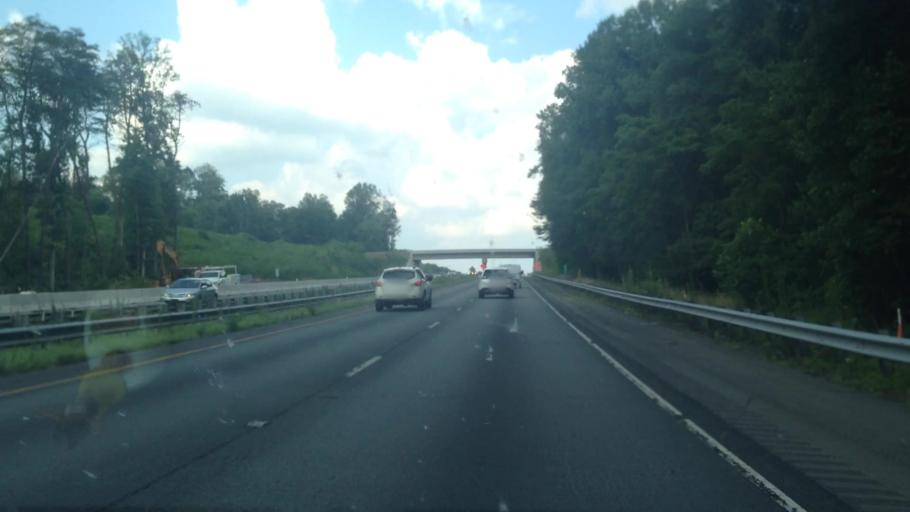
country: US
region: North Carolina
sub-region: Forsyth County
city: Walkertown
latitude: 36.1137
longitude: -80.1470
